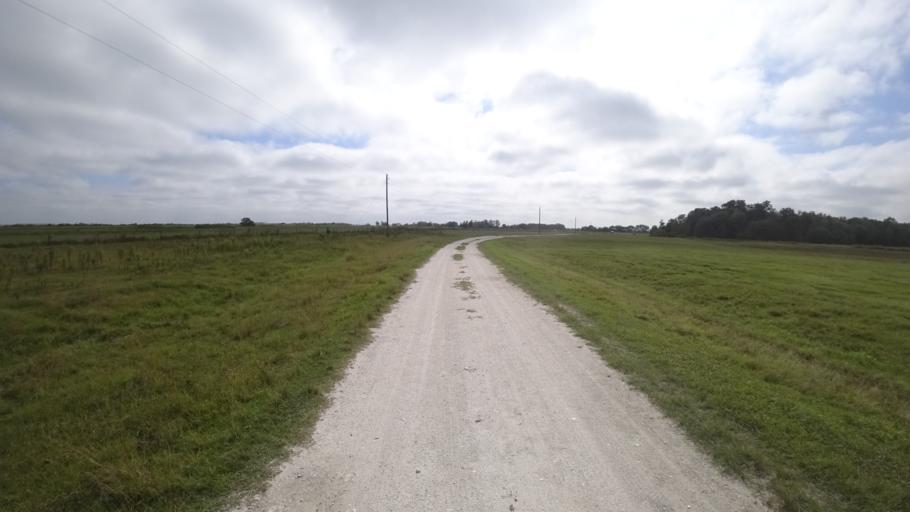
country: US
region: Florida
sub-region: DeSoto County
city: Arcadia
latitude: 27.3212
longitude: -82.1096
